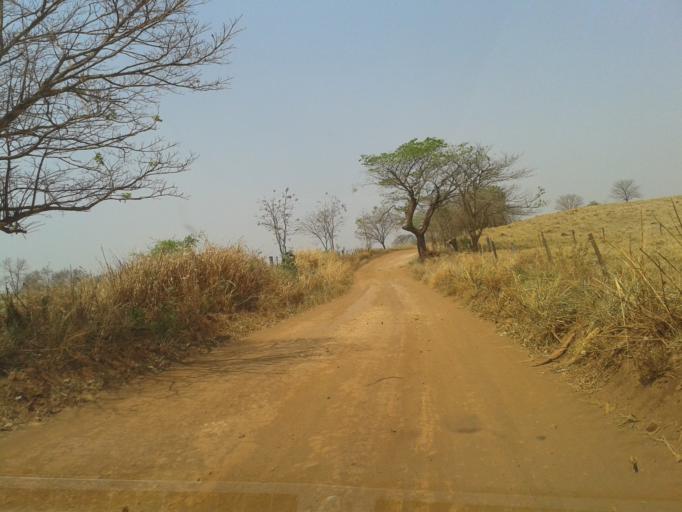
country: BR
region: Minas Gerais
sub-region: Centralina
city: Centralina
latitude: -18.7062
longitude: -49.2357
